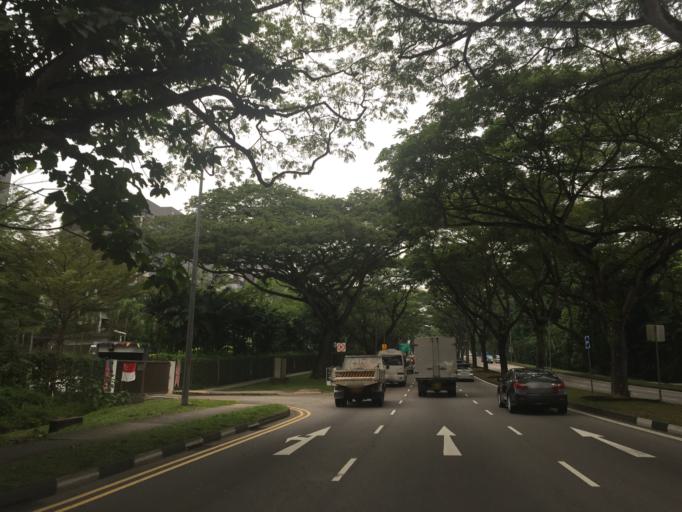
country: SG
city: Singapore
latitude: 1.3816
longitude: 103.8265
